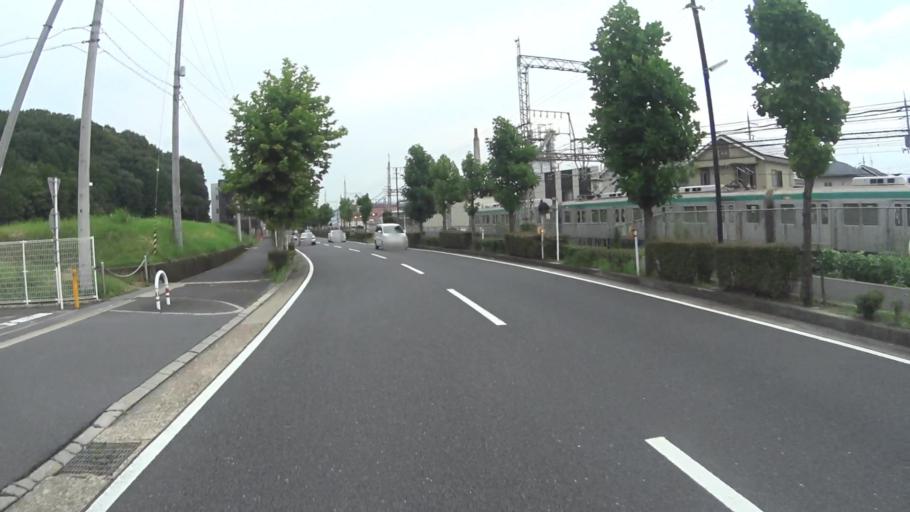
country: JP
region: Nara
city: Nara-shi
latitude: 34.7389
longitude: 135.7938
